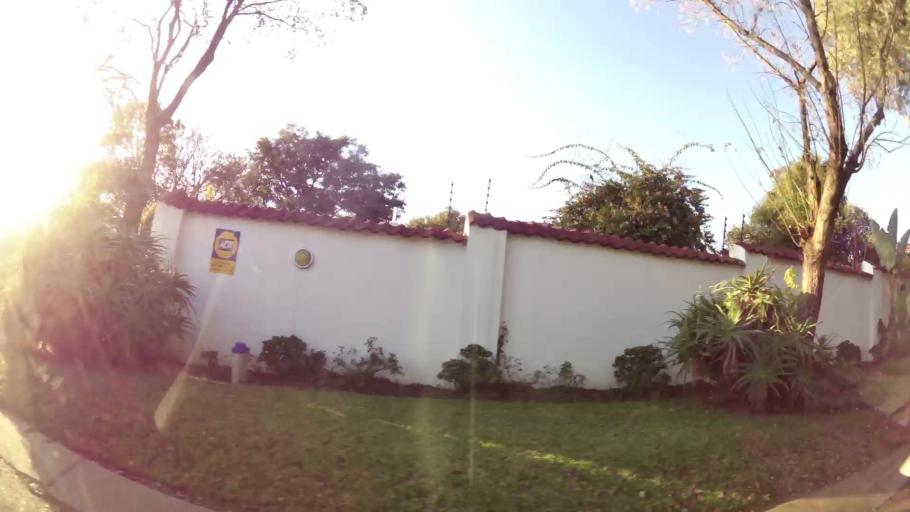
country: ZA
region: Gauteng
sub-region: City of Johannesburg Metropolitan Municipality
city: Modderfontein
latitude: -26.0743
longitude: 28.0739
